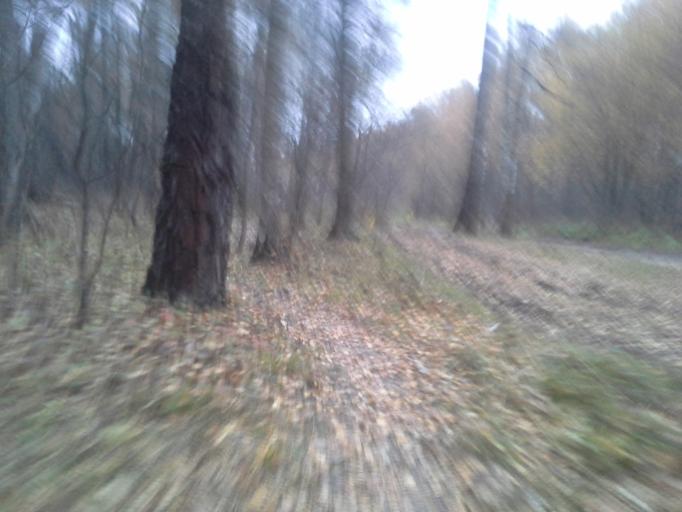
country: RU
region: Moskovskaya
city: Kommunarka
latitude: 55.5512
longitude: 37.4662
